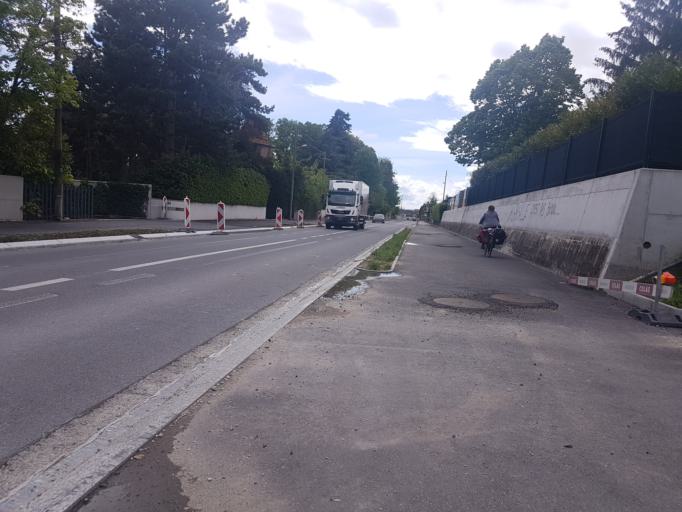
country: CH
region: Vaud
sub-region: Nyon District
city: Coppet
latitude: 46.3221
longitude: 6.1967
